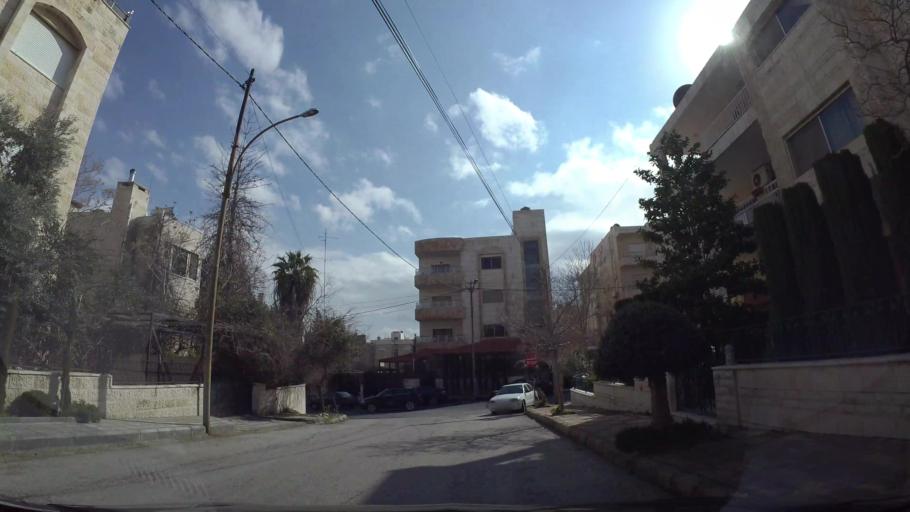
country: JO
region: Amman
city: Amman
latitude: 31.9717
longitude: 35.8908
